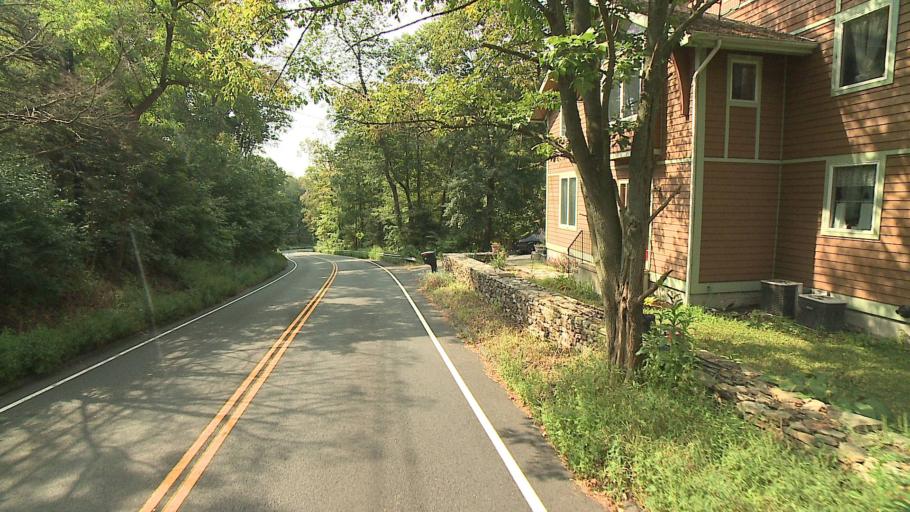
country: US
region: Connecticut
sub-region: Fairfield County
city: Georgetown
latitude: 41.2988
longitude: -73.3885
